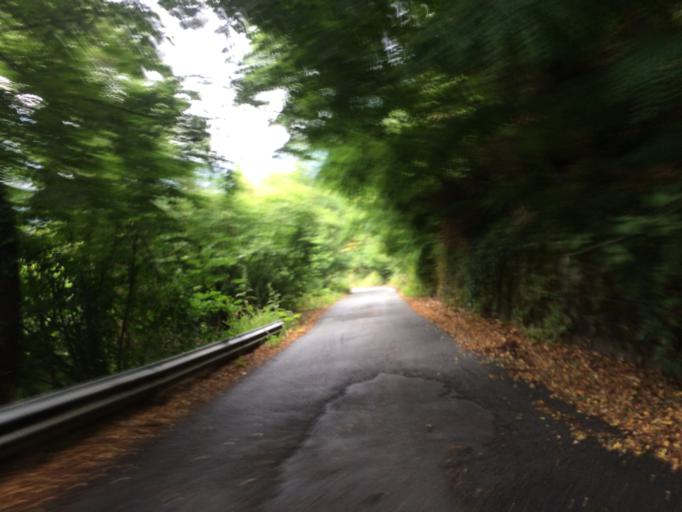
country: IT
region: Liguria
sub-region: Provincia di Imperia
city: Castel Vittorio
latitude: 43.9445
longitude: 7.6897
